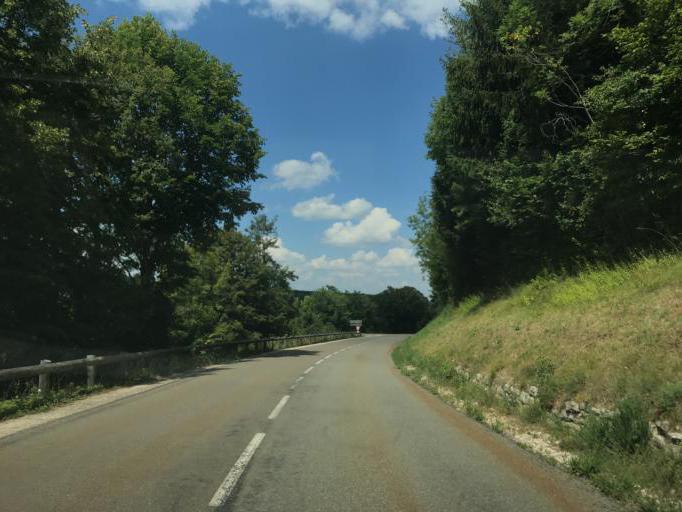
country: FR
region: Franche-Comte
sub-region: Departement du Jura
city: Clairvaux-les-Lacs
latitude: 46.5639
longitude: 5.7603
